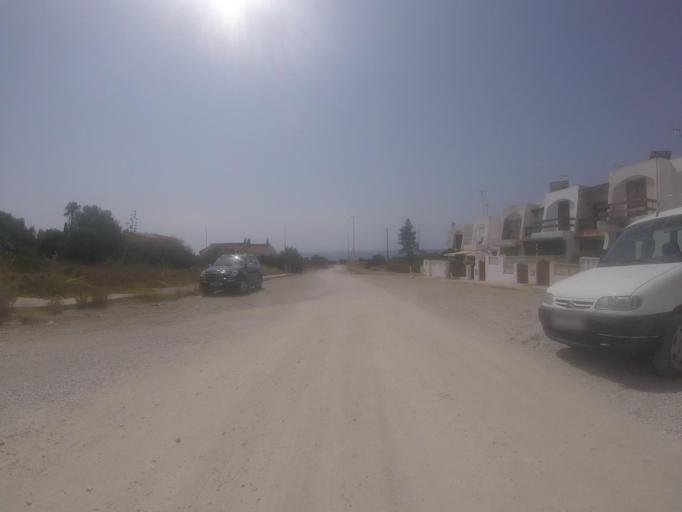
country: ES
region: Valencia
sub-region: Provincia de Castello
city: Peniscola
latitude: 40.3428
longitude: 0.3764
